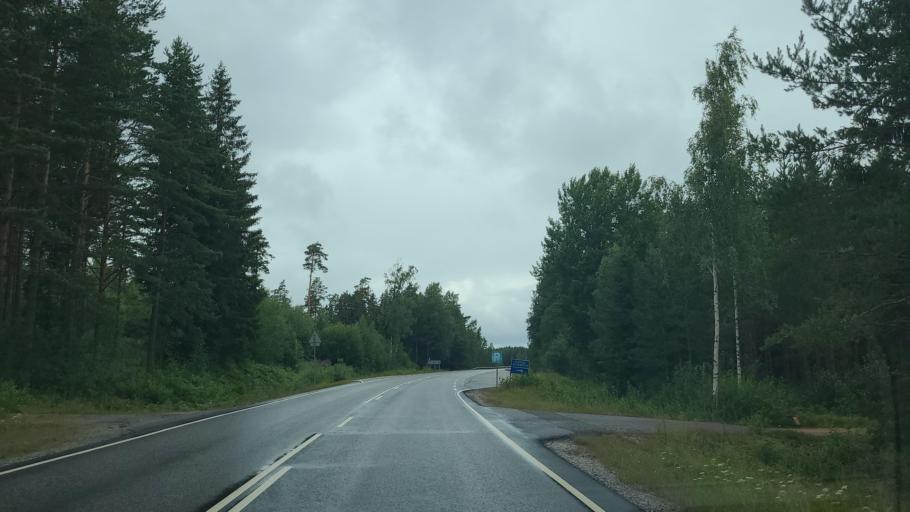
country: FI
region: Varsinais-Suomi
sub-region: Aboland-Turunmaa
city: Kimito
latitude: 60.2269
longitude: 22.6155
